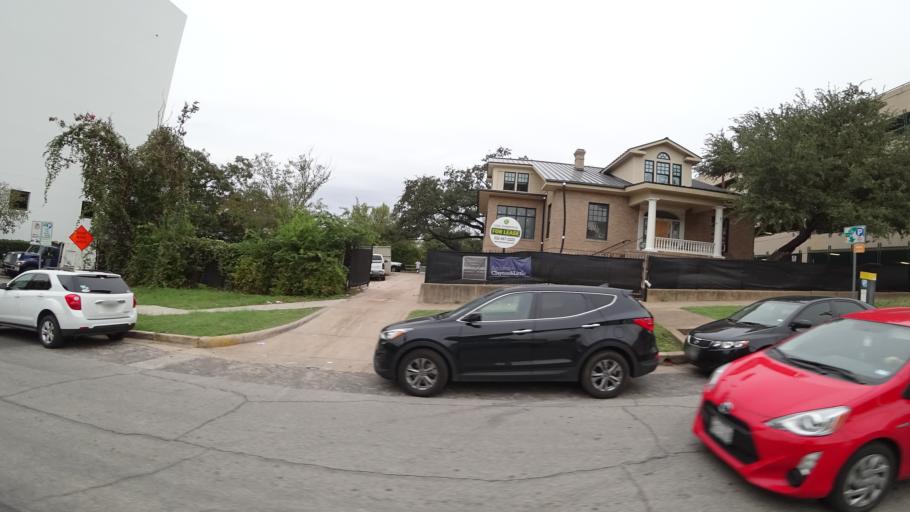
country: US
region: Texas
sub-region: Travis County
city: Austin
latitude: 30.2724
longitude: -97.7463
